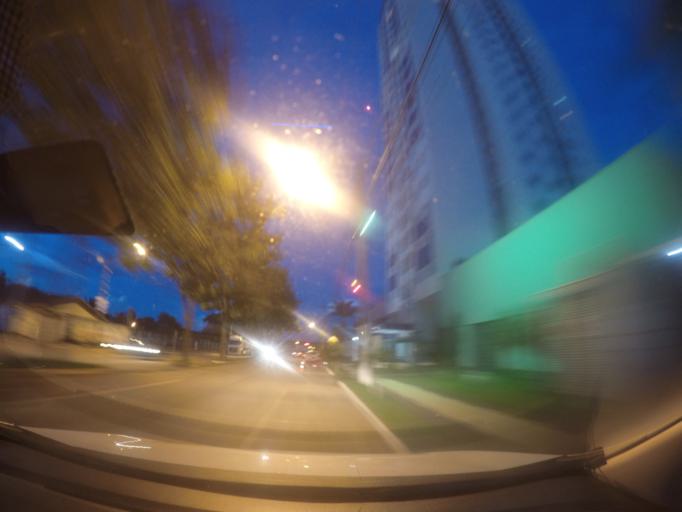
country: BR
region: Goias
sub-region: Inhumas
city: Inhumas
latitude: -16.3675
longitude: -49.4988
